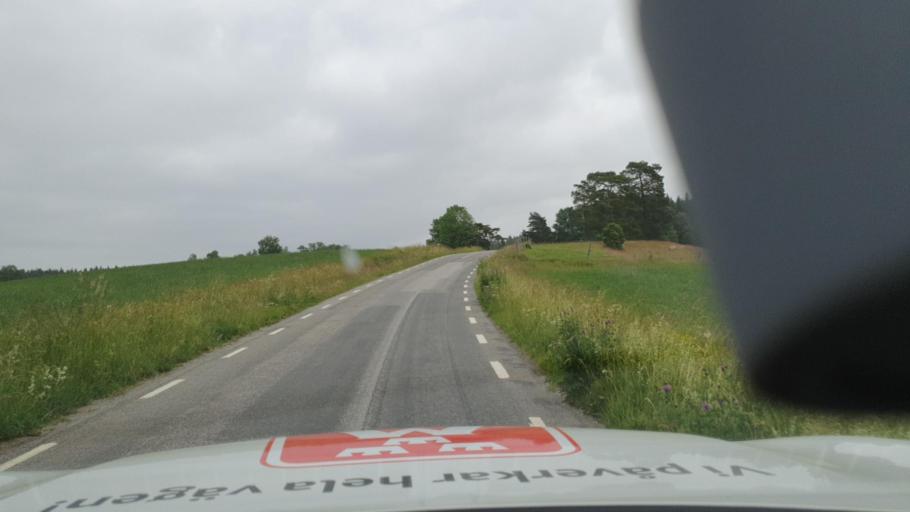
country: SE
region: Vaestra Goetaland
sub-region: Falkopings Kommun
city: Falkoeping
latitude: 57.9820
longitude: 13.5517
